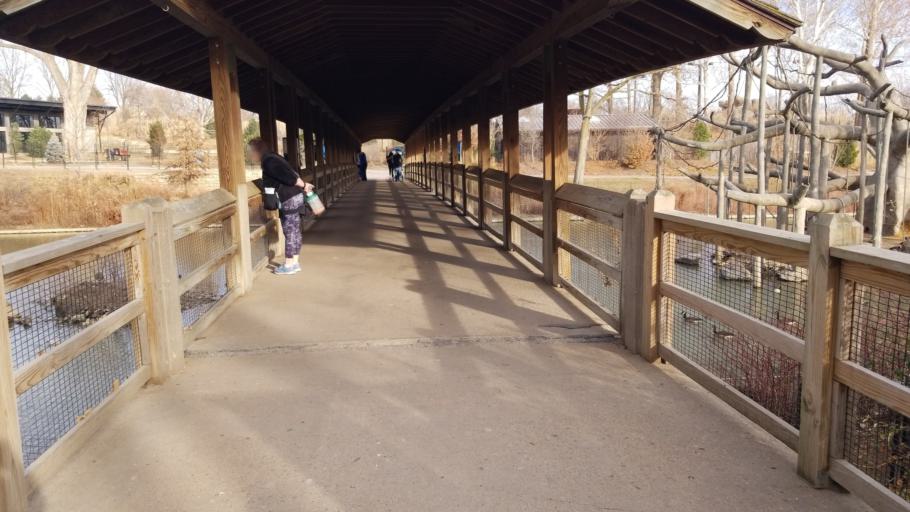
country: US
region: Nebraska
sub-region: Douglas County
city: Omaha
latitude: 41.2255
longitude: -95.9244
